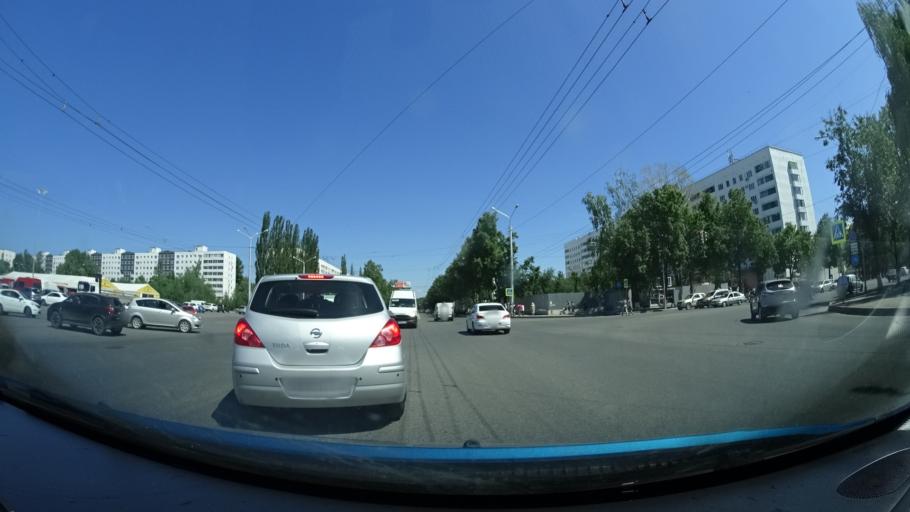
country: RU
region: Bashkortostan
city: Ufa
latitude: 54.7589
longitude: 55.9971
